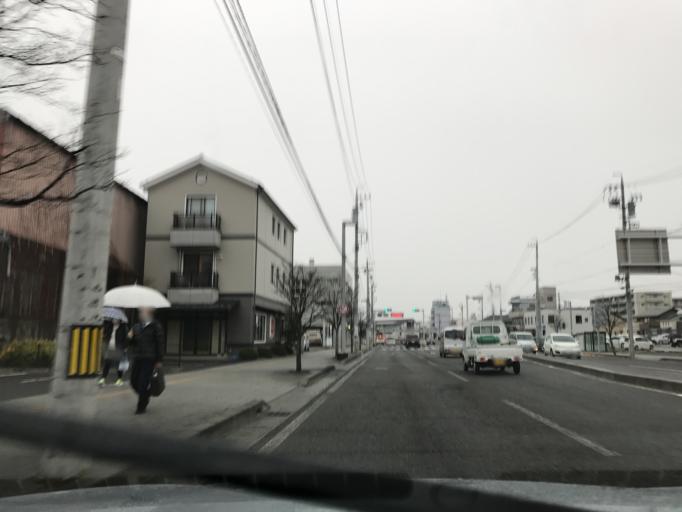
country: JP
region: Nagano
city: Matsumoto
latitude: 36.2372
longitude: 137.9649
